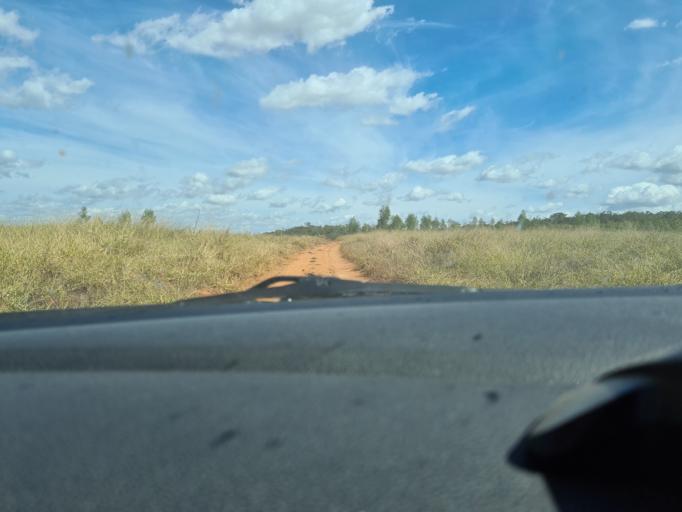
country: BR
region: Goias
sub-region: Silvania
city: Silvania
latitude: -16.5289
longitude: -48.5476
